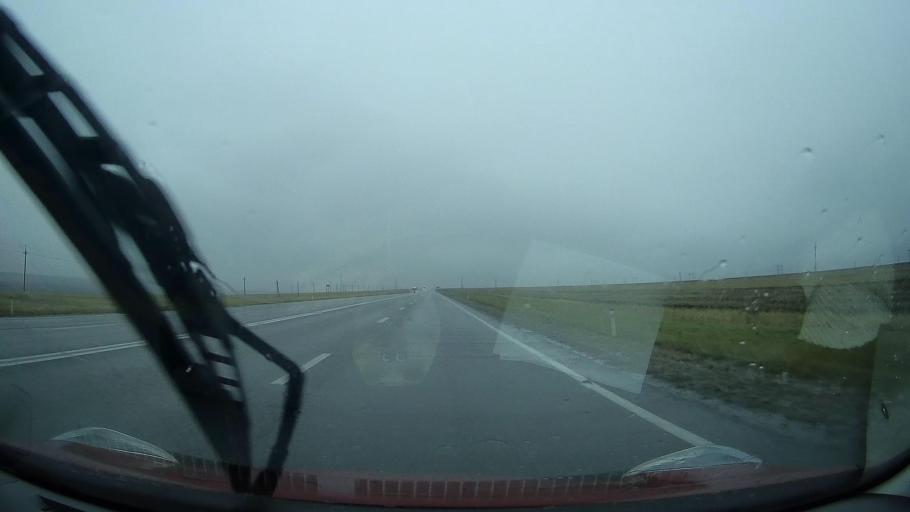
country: RU
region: Stavropol'skiy
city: Kursavka
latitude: 44.5813
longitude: 42.2420
